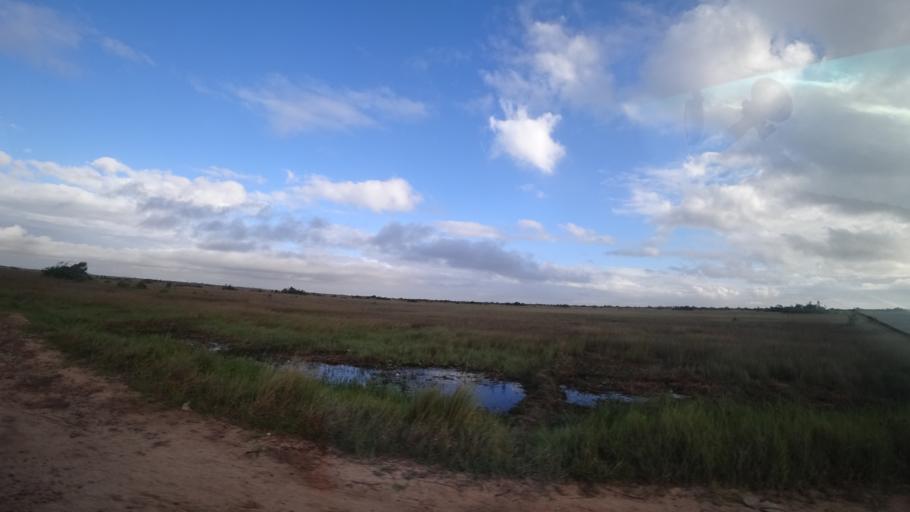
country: MZ
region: Sofala
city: Beira
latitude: -19.7038
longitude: 35.0221
